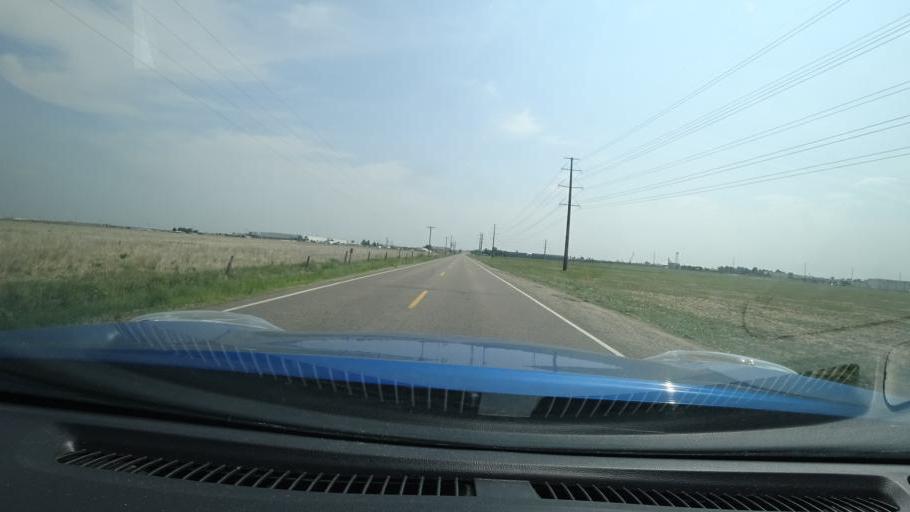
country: US
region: Colorado
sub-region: Adams County
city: Aurora
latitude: 39.7605
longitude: -104.7347
